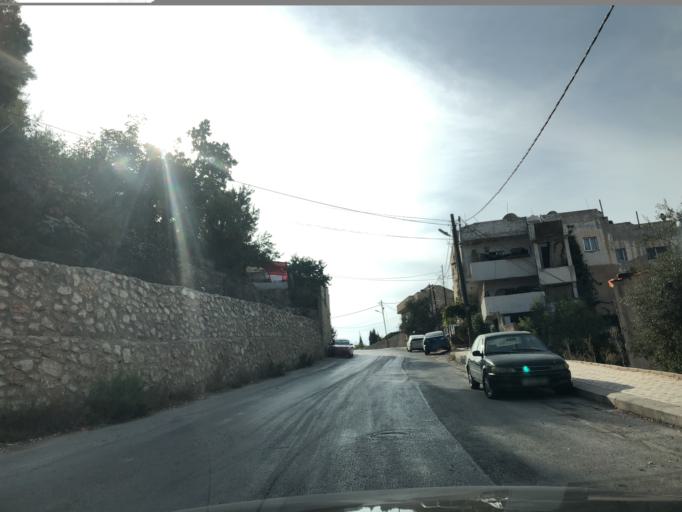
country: JO
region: Irbid
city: `Ayn Jannah
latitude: 32.3316
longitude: 35.7642
